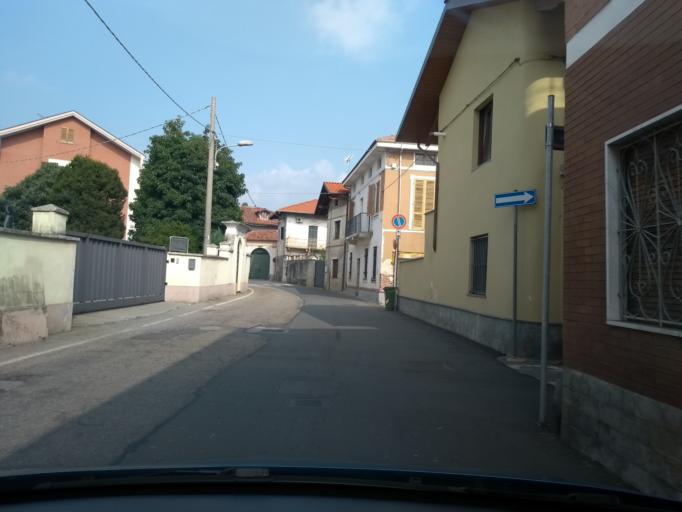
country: IT
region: Piedmont
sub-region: Provincia di Torino
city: Favria
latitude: 45.3336
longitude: 7.6894
